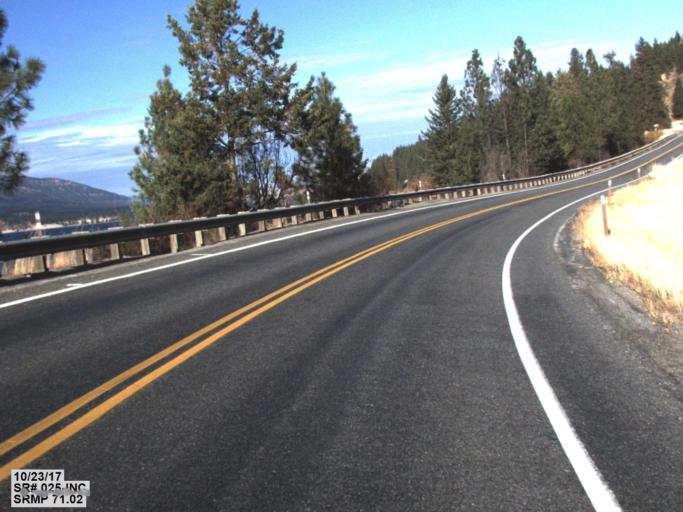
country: US
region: Washington
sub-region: Stevens County
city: Kettle Falls
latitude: 48.4890
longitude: -118.1668
